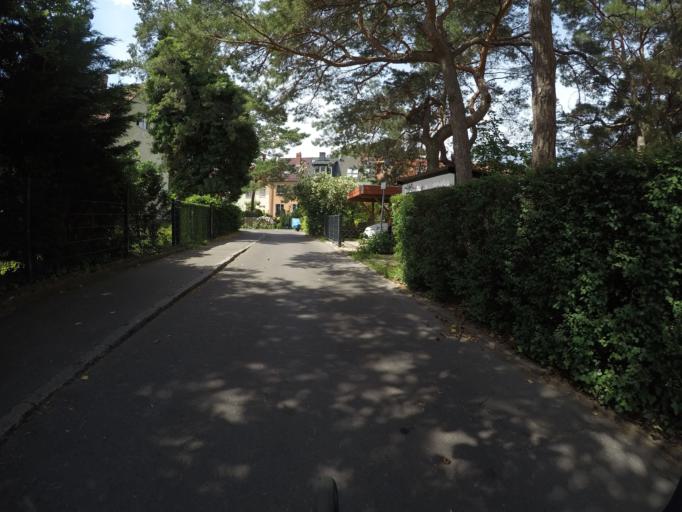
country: DE
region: Berlin
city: Adlershof
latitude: 52.4405
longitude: 13.5406
